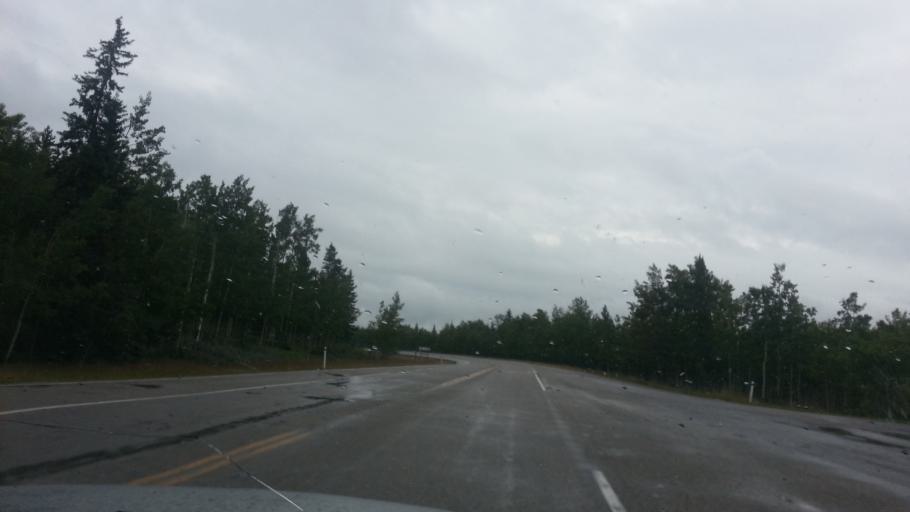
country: CA
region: Alberta
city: Cochrane
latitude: 50.8784
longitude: -114.7167
